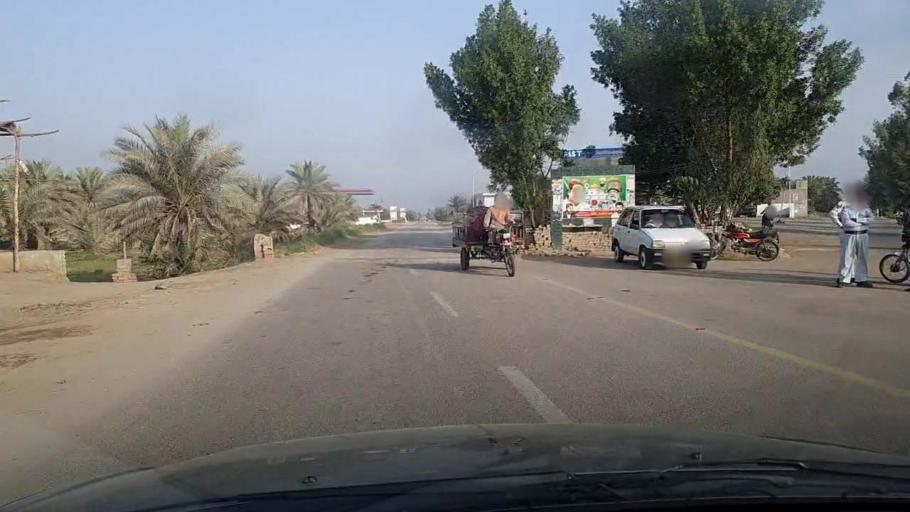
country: PK
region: Sindh
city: Khairpur
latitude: 27.5394
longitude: 68.7101
